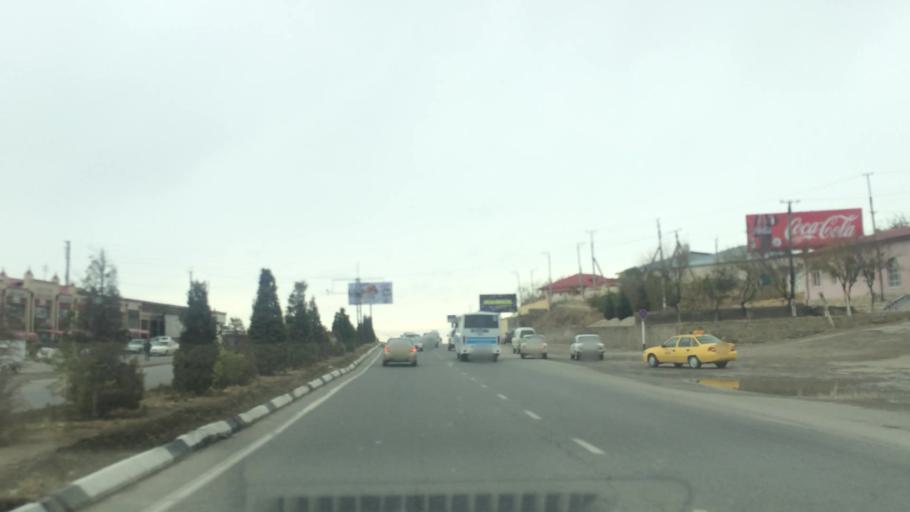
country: UZ
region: Samarqand
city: Samarqand
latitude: 39.6760
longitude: 67.0118
